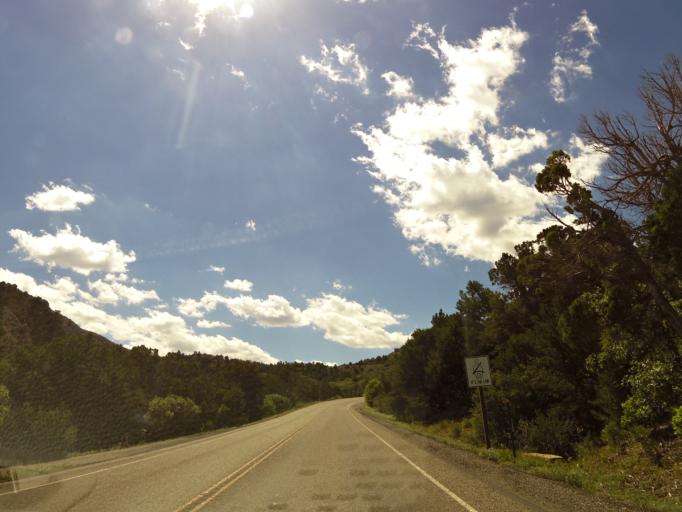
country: US
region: Colorado
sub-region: Montezuma County
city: Mancos
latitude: 37.3268
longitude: -108.4175
